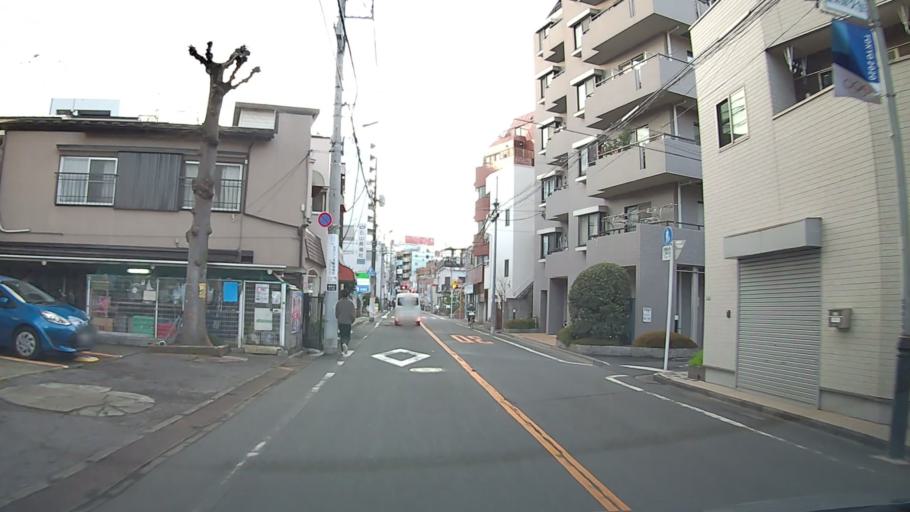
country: JP
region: Tokyo
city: Tokyo
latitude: 35.7372
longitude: 139.6580
